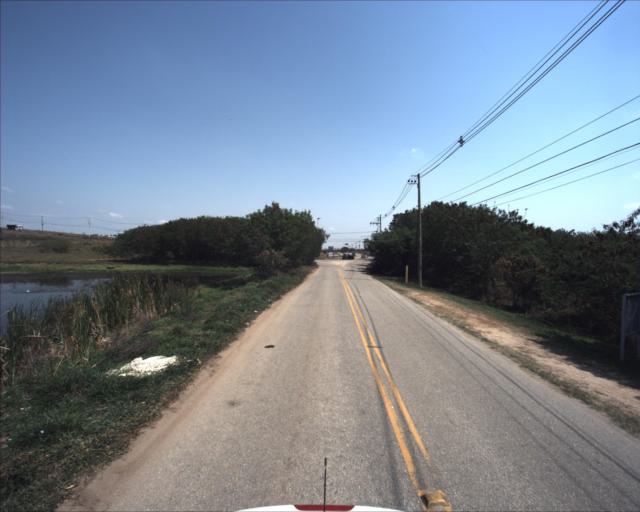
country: BR
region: Sao Paulo
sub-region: Sorocaba
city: Sorocaba
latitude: -23.4279
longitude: -47.4473
